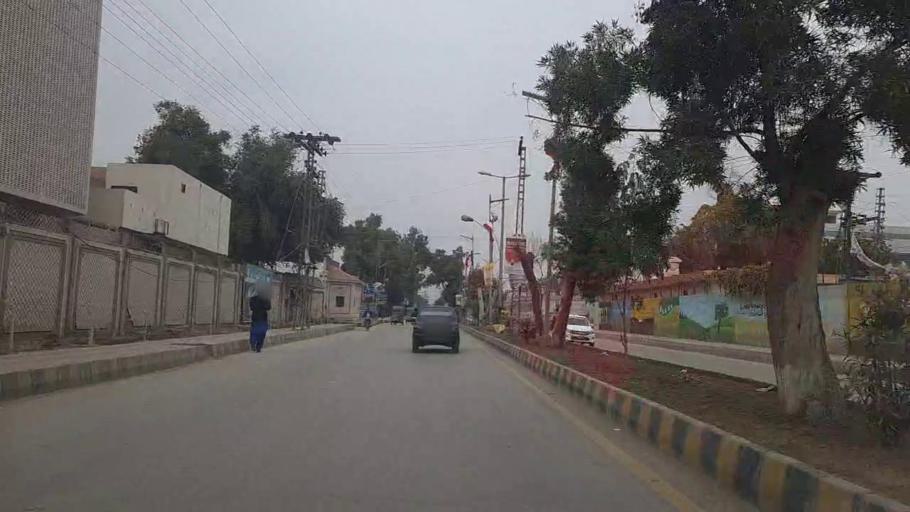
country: PK
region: Sindh
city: Nawabshah
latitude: 26.2442
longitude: 68.4017
